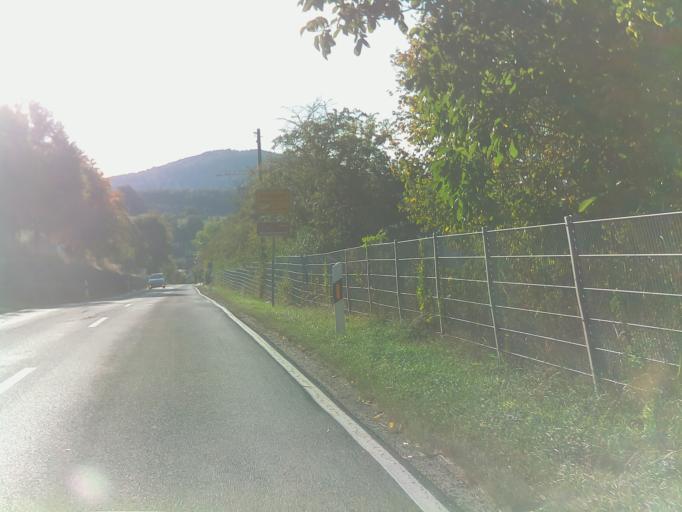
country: DE
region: Thuringia
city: Stepfershausen
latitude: 50.5548
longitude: 10.2910
